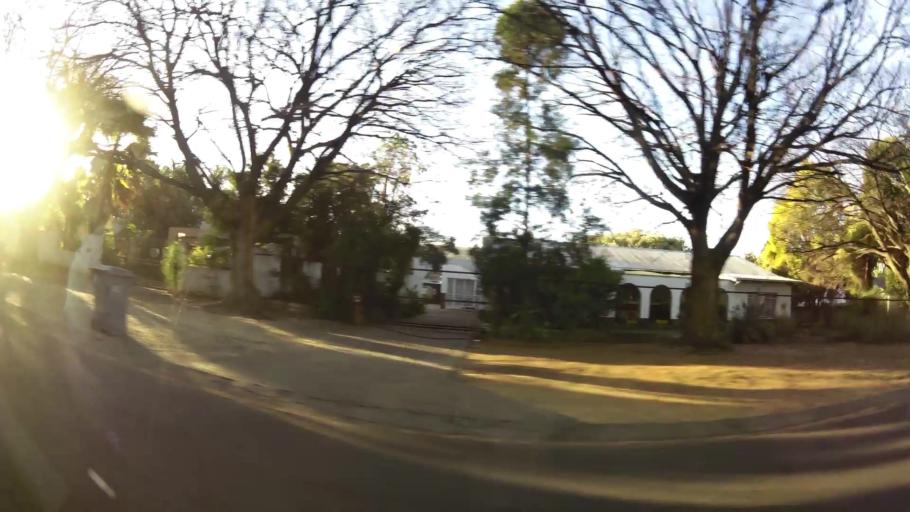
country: ZA
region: Gauteng
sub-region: City of Tshwane Metropolitan Municipality
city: Pretoria
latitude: -25.7034
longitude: 28.2634
